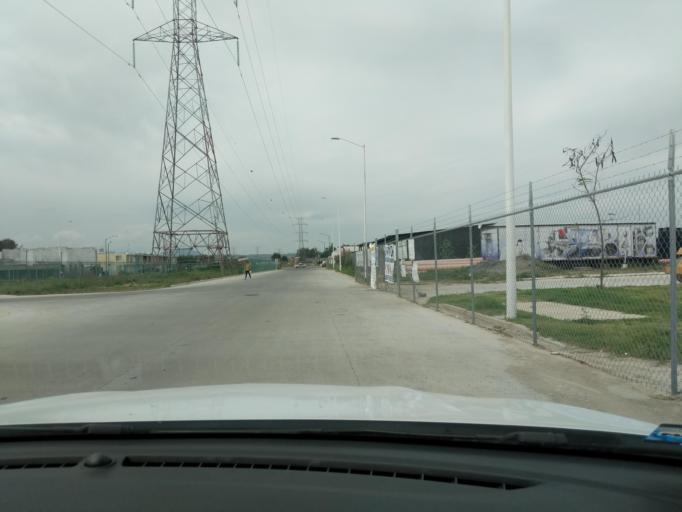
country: MX
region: Jalisco
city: Tesistan
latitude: 20.7855
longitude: -103.4875
